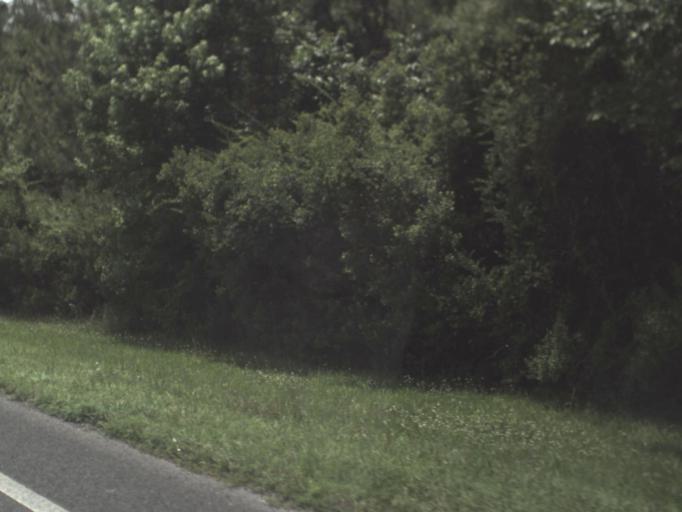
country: US
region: Florida
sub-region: Nassau County
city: Callahan
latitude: 30.6064
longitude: -81.8370
